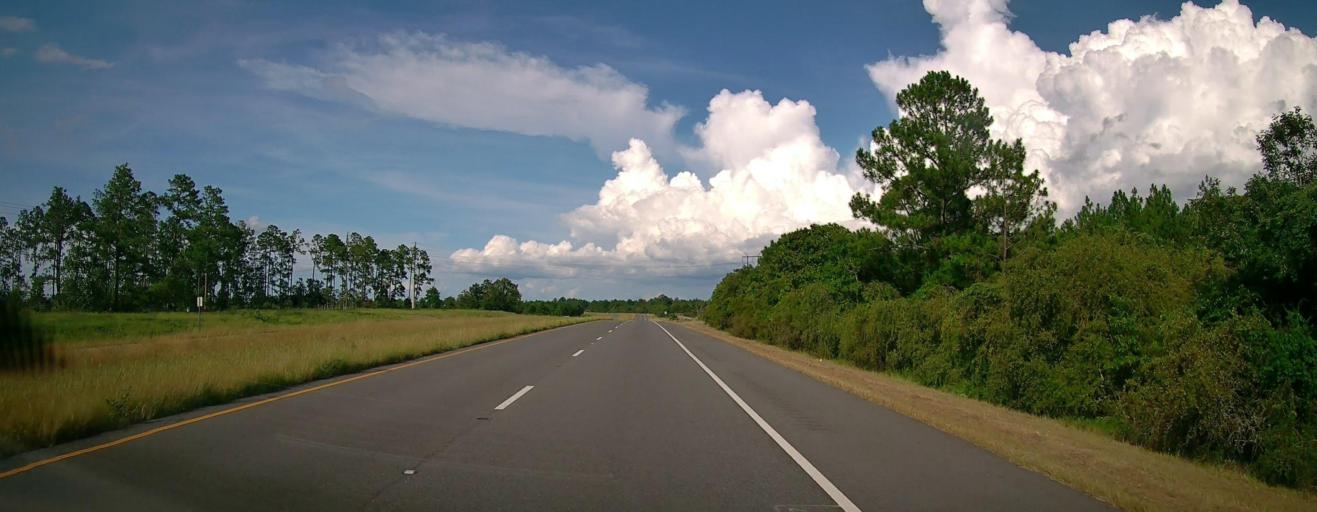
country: US
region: Georgia
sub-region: Talbot County
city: Talbotton
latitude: 32.5889
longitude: -84.5027
